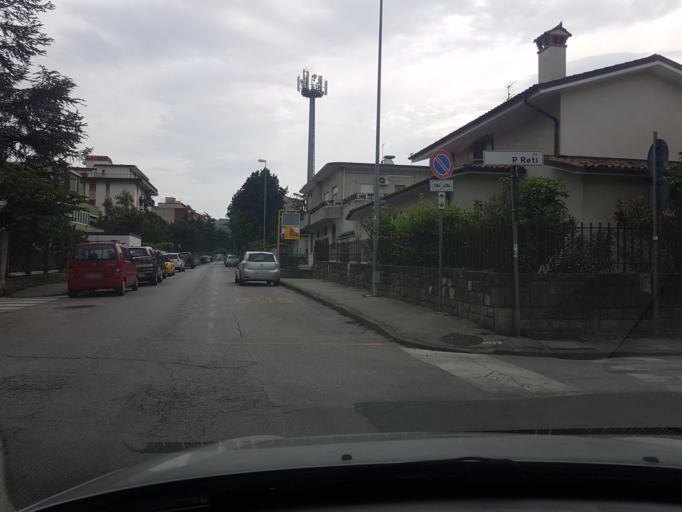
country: IT
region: Friuli Venezia Giulia
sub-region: Provincia di Trieste
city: Muggia
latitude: 45.6002
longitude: 13.7677
